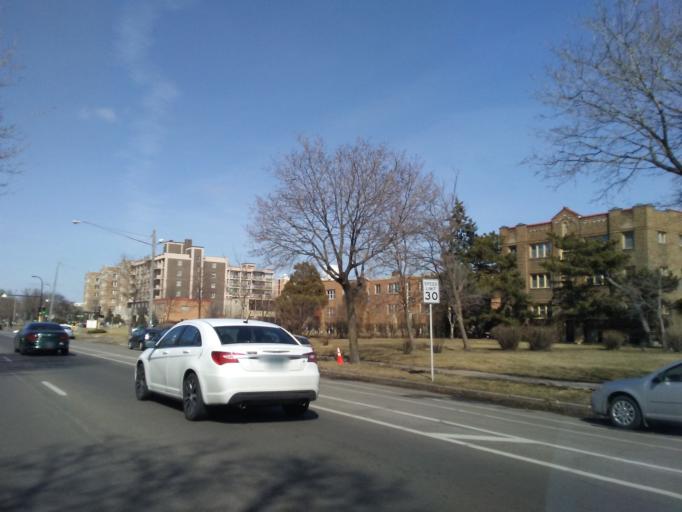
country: US
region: Minnesota
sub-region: Hennepin County
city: Minneapolis
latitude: 44.9528
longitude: -93.2652
